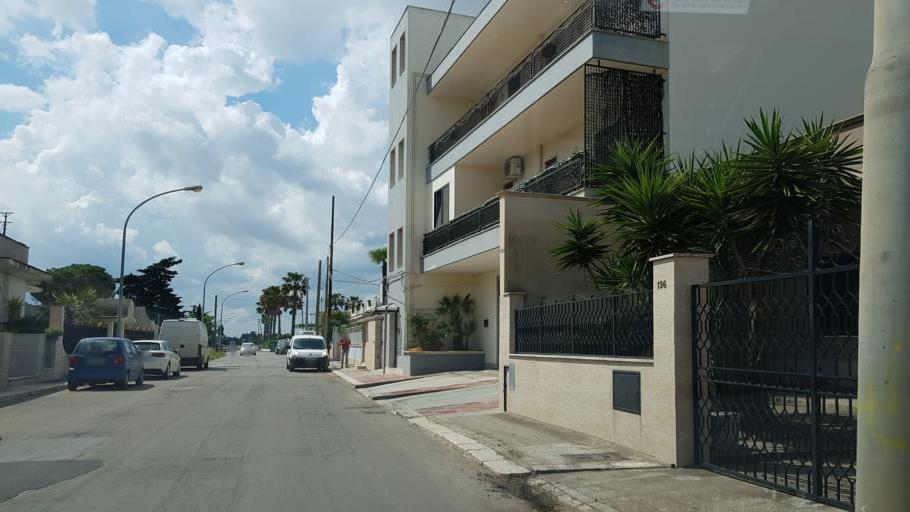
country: IT
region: Apulia
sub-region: Provincia di Brindisi
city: Mesagne
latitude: 40.5500
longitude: 17.8128
